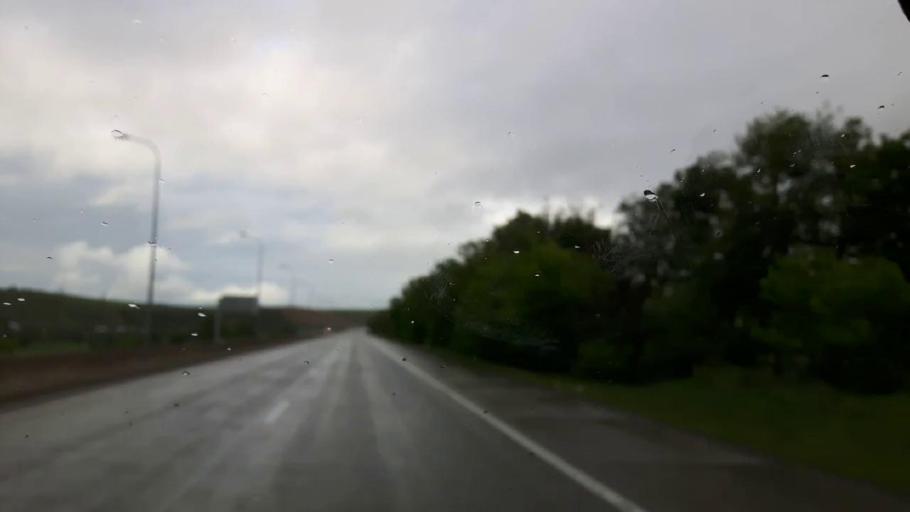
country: GE
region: Shida Kartli
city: Kaspi
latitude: 42.0016
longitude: 44.3798
